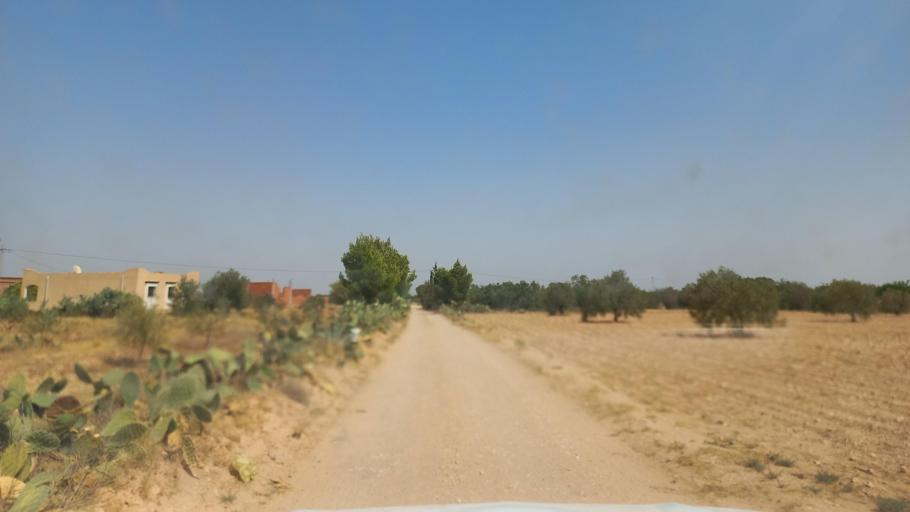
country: TN
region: Al Qasrayn
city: Kasserine
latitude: 35.2495
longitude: 9.0092
